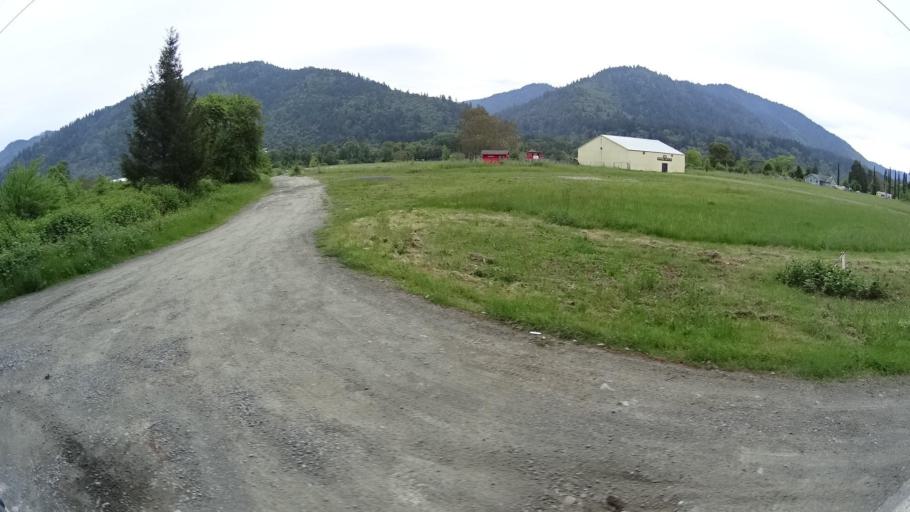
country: US
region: California
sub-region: Humboldt County
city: Willow Creek
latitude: 41.0751
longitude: -123.6947
